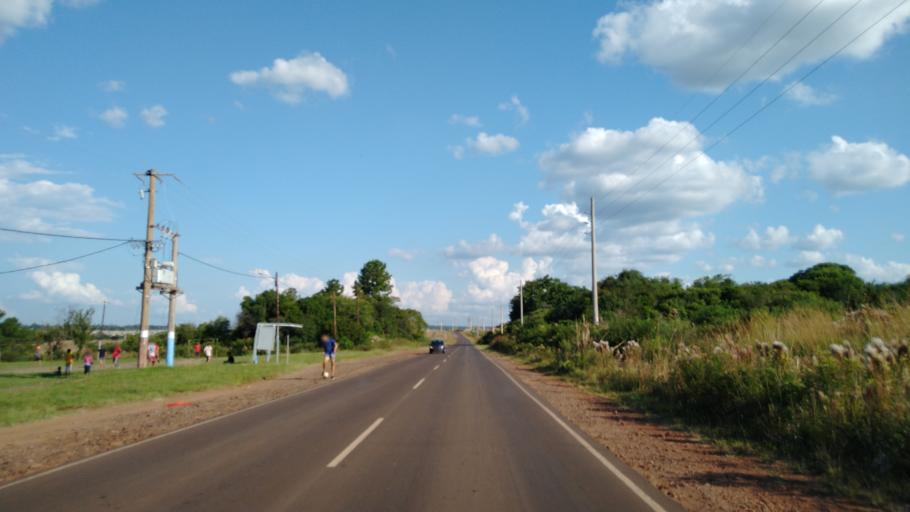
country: PY
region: Itapua
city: San Juan del Parana
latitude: -27.3853
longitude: -55.9914
